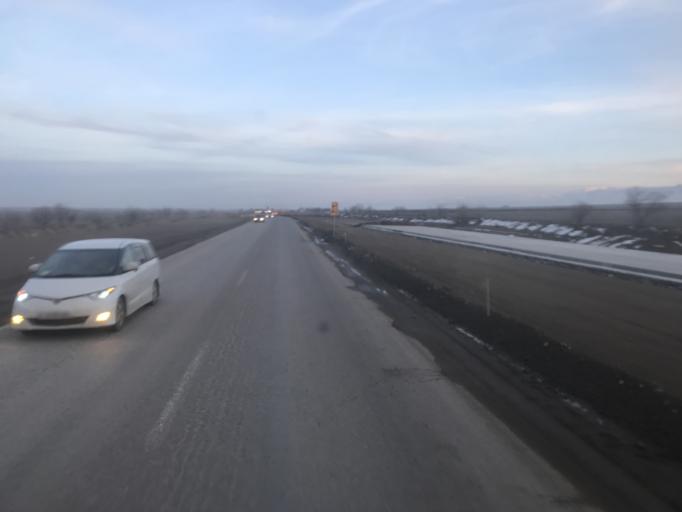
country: KG
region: Chuy
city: Ivanovka
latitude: 43.3728
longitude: 75.2772
